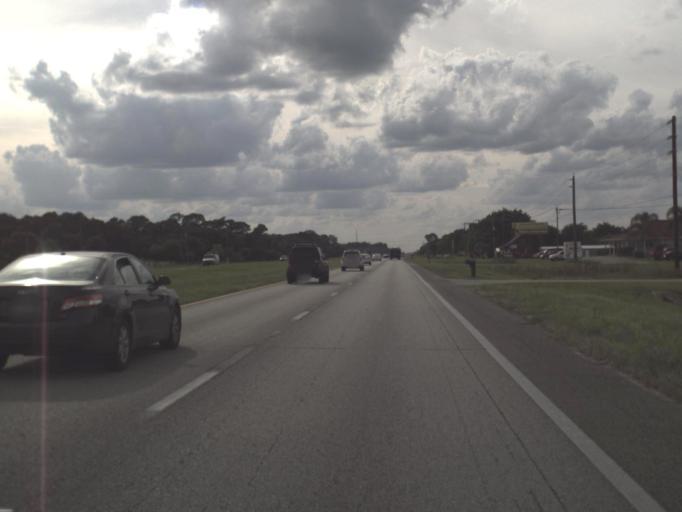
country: US
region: Florida
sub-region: Lee County
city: Alva
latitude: 26.7099
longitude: -81.5261
